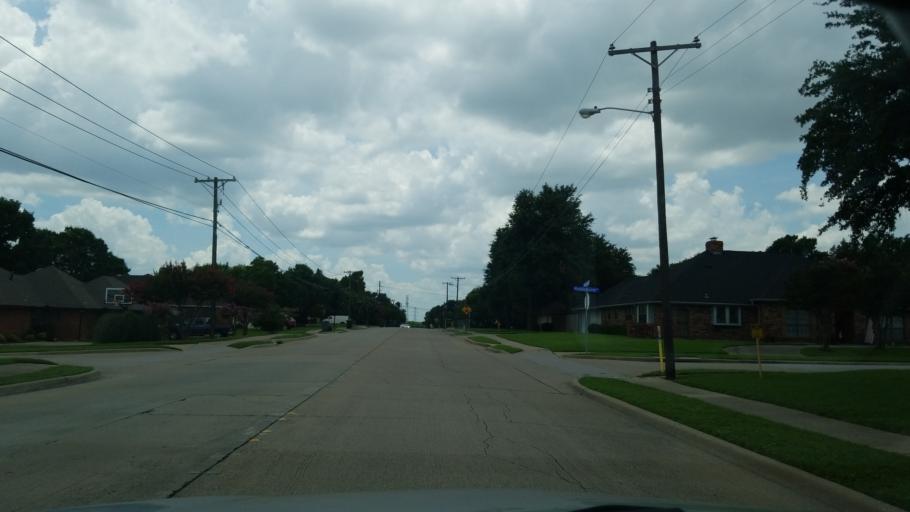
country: US
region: Texas
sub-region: Dallas County
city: Coppell
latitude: 32.9619
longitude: -96.9767
